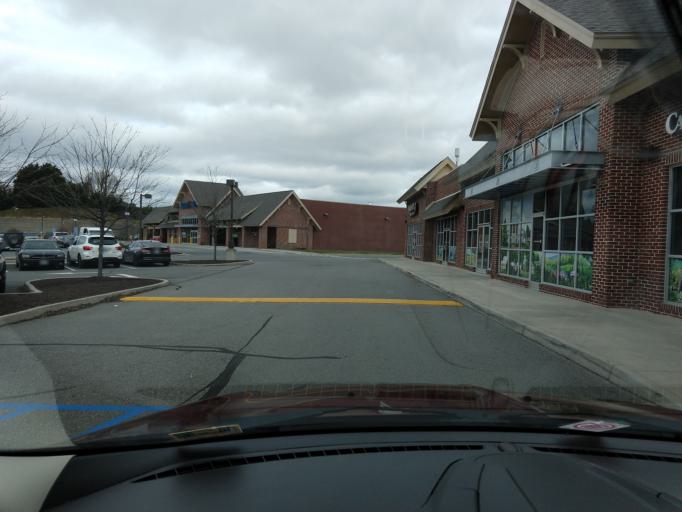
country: US
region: Virginia
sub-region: Botetourt County
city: Daleville
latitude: 37.4168
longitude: -79.9098
